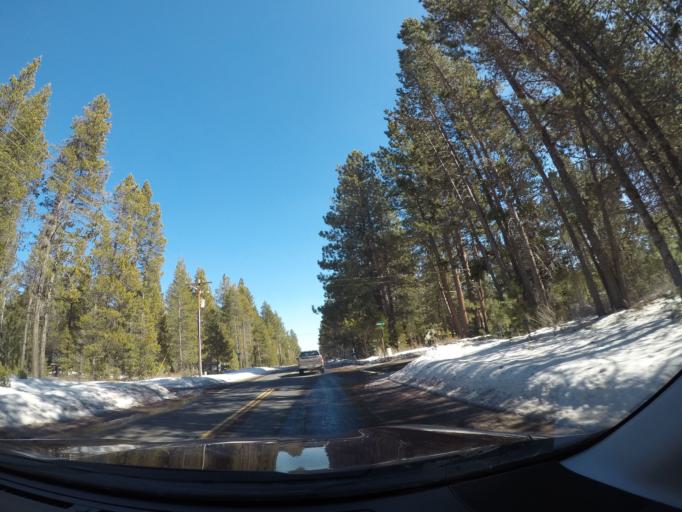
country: US
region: Oregon
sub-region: Deschutes County
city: Three Rivers
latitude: 43.8629
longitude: -121.4765
